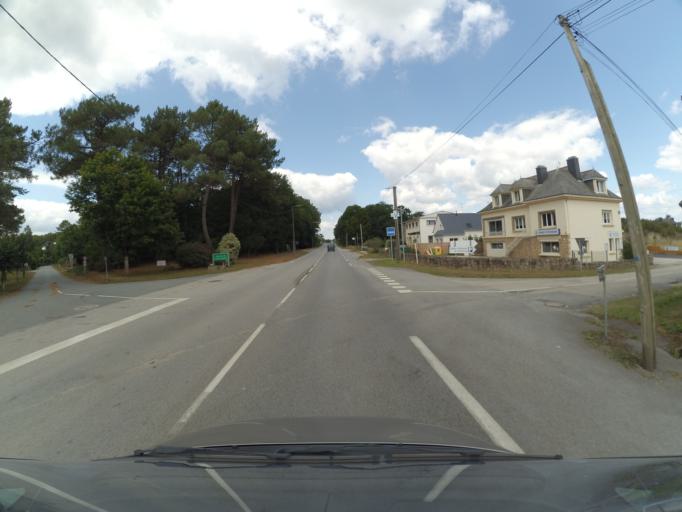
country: FR
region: Brittany
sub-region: Departement du Morbihan
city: Brech
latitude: 47.7125
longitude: -3.0078
